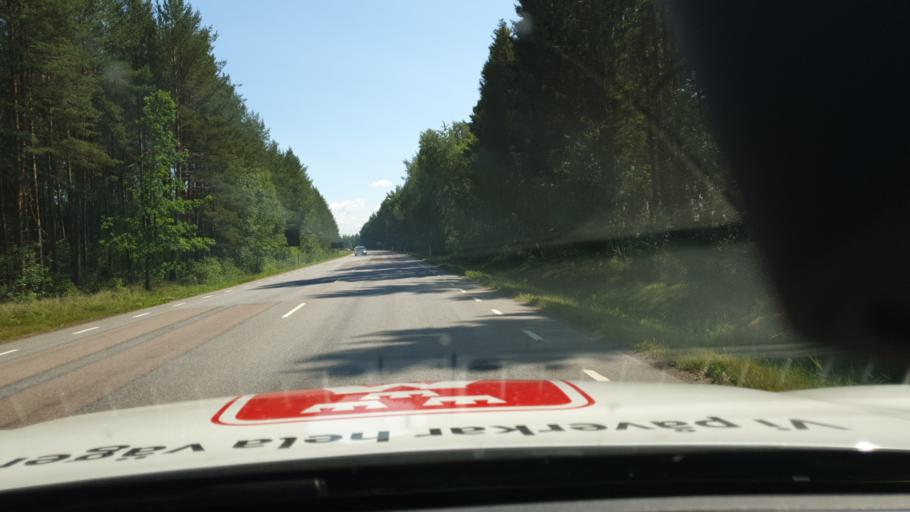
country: SE
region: Vaestra Goetaland
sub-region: Lidkopings Kommun
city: Lidkoping
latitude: 58.5161
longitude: 13.1148
